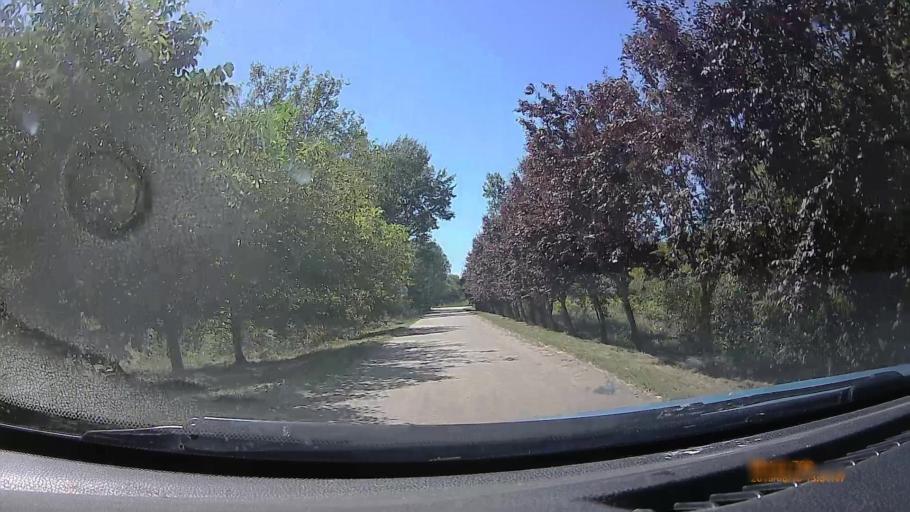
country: HU
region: Fejer
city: Cece
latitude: 46.8082
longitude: 18.5845
